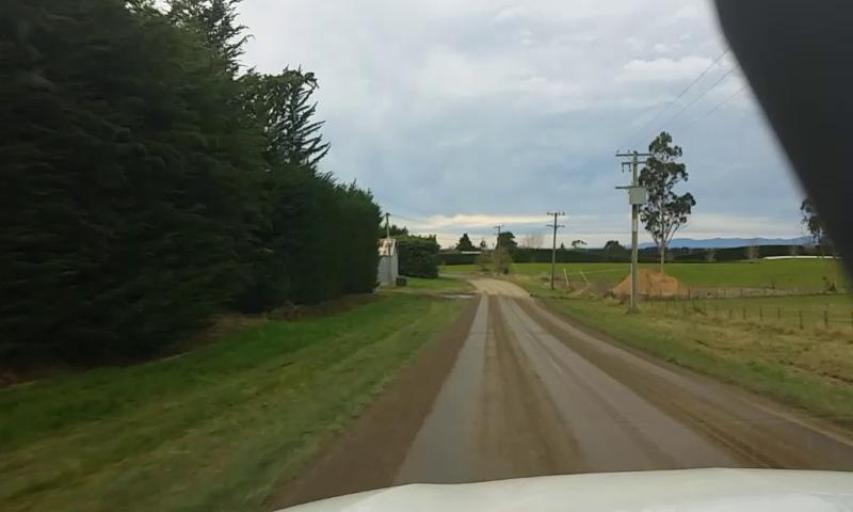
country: NZ
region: Canterbury
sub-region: Waimakariri District
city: Kaiapoi
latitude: -43.2994
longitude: 172.4822
